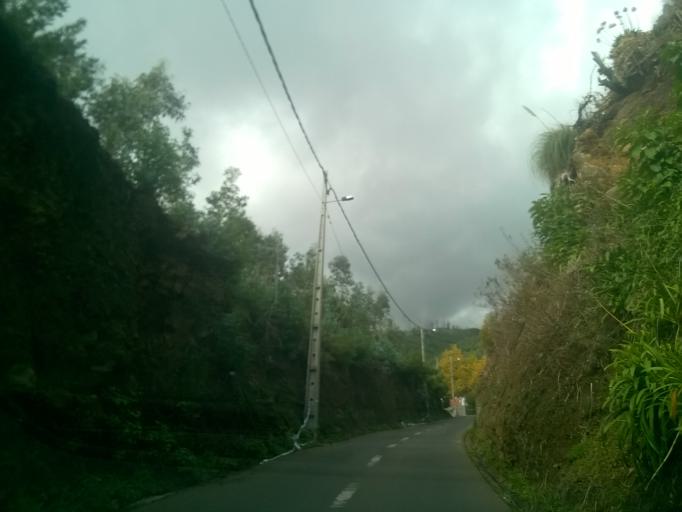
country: PT
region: Madeira
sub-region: Funchal
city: Nossa Senhora do Monte
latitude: 32.6763
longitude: -16.8992
